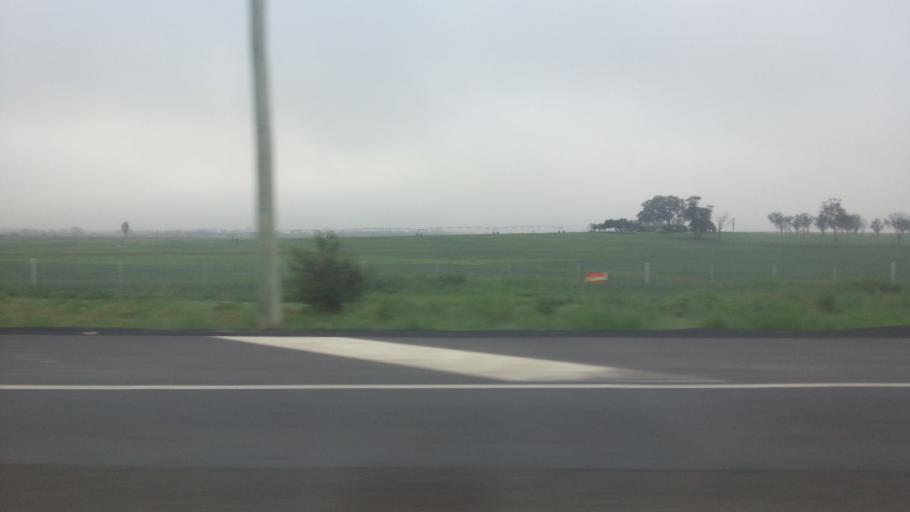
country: AU
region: New South Wales
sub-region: Liverpool
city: Bringelly
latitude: -33.9749
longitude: 150.7357
